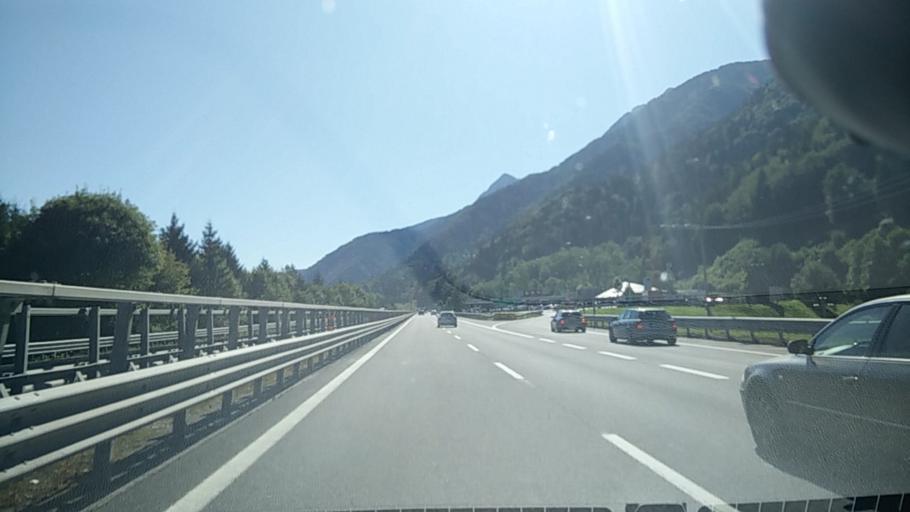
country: IT
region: Friuli Venezia Giulia
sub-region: Provincia di Udine
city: Pontebba
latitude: 46.4997
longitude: 13.3724
